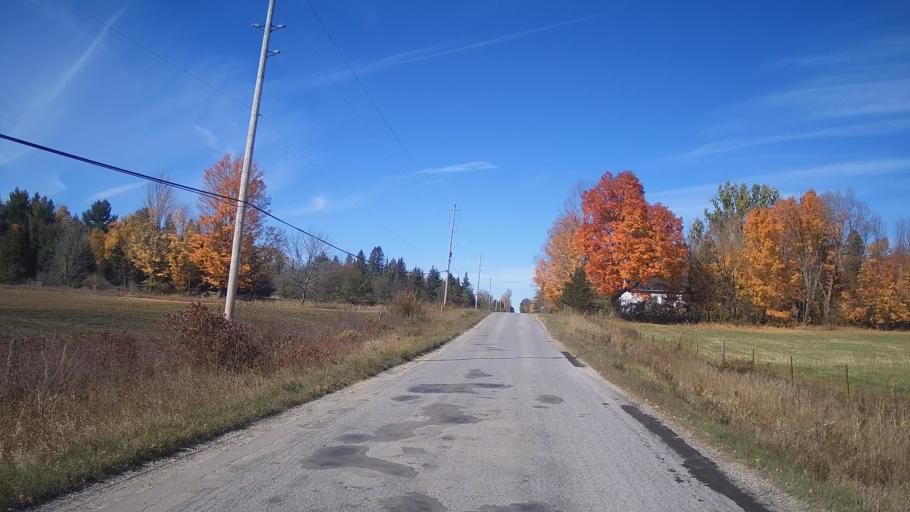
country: CA
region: Ontario
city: Perth
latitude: 44.8481
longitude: -76.3688
